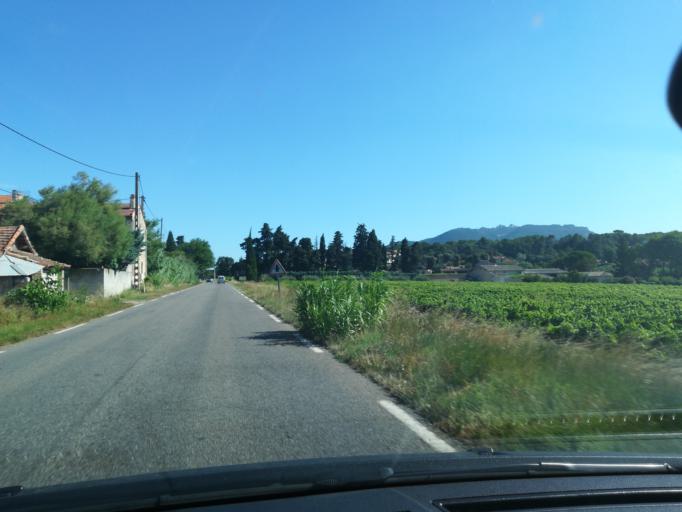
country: FR
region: Provence-Alpes-Cote d'Azur
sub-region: Departement du Vaucluse
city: Vacqueyras
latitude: 44.1132
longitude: 4.9786
